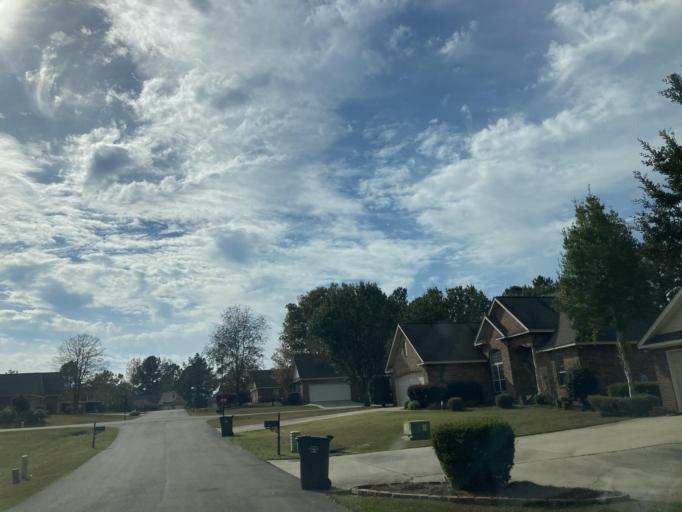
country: US
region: Mississippi
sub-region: Lamar County
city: West Hattiesburg
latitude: 31.3326
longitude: -89.4331
